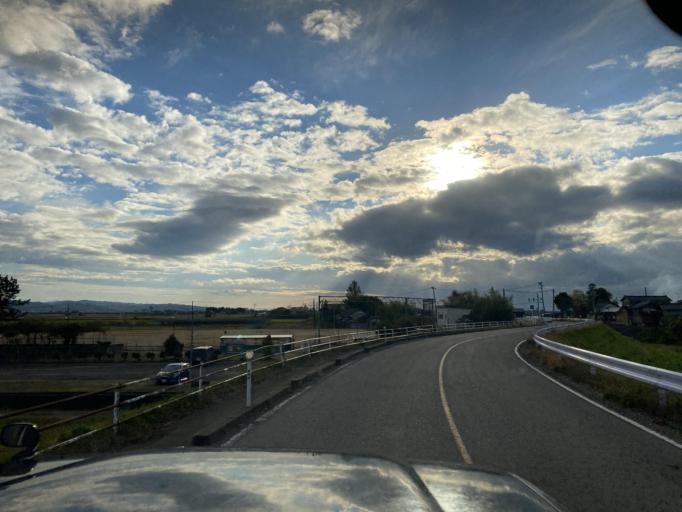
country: JP
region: Niigata
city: Kamo
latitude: 37.6828
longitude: 139.0216
